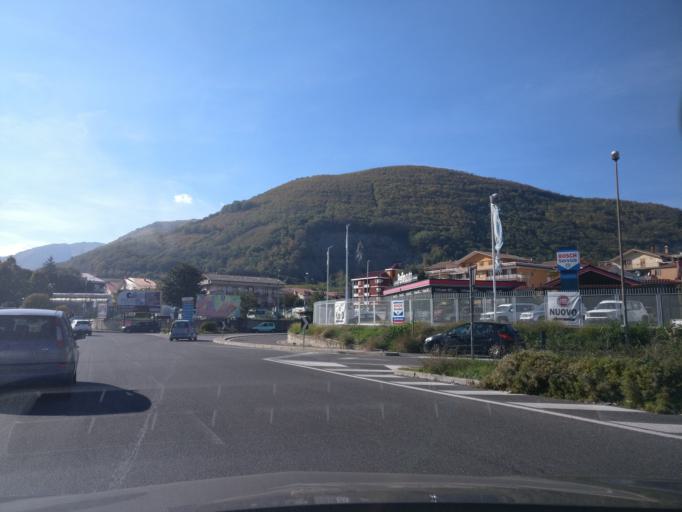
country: IT
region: Campania
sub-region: Provincia di Avellino
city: Torelli-Torrette
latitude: 40.9073
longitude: 14.7484
